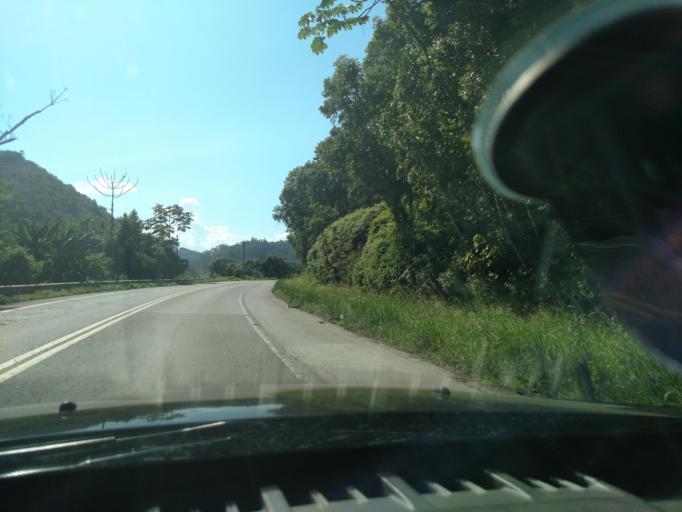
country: BR
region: Santa Catarina
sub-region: Ibirama
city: Ibirama
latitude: -27.0858
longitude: -49.4792
